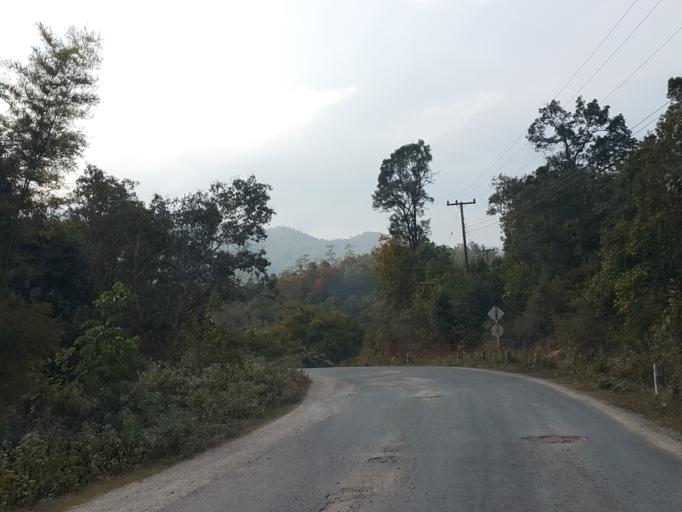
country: TH
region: Chiang Mai
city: Om Koi
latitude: 17.8139
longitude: 98.3300
